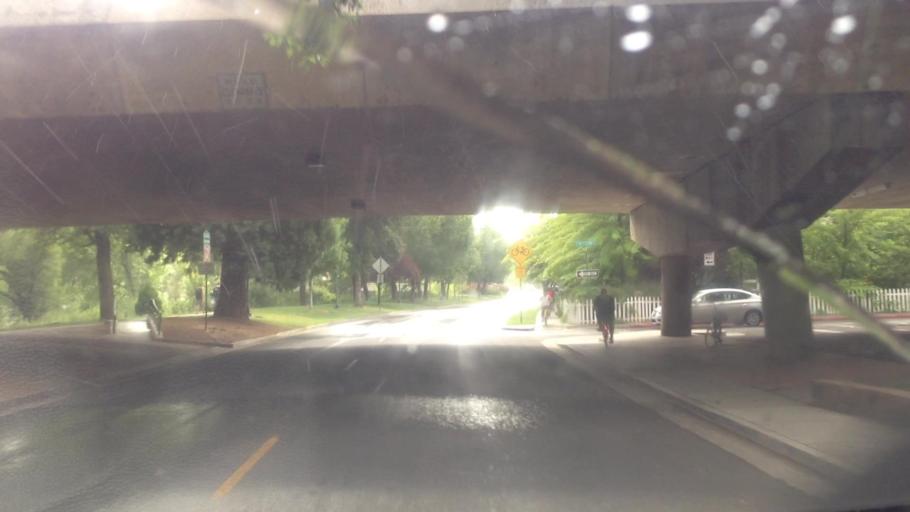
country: US
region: Nevada
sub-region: Washoe County
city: Reno
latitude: 39.5207
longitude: -119.8242
